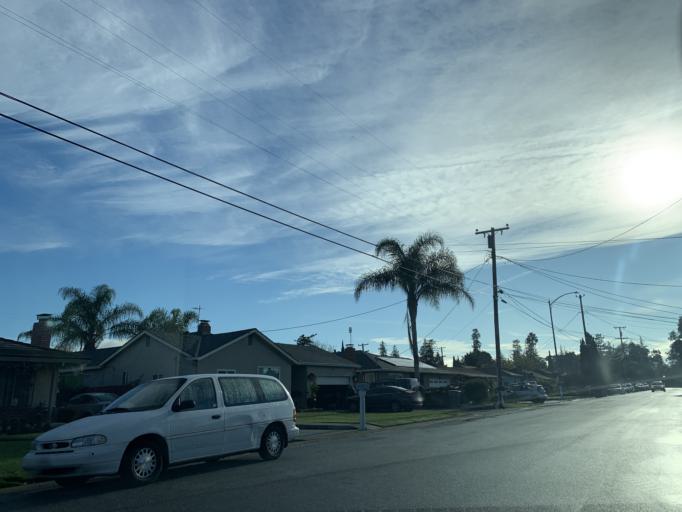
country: US
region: California
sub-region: Santa Clara County
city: San Jose
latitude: 37.3392
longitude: -121.8587
